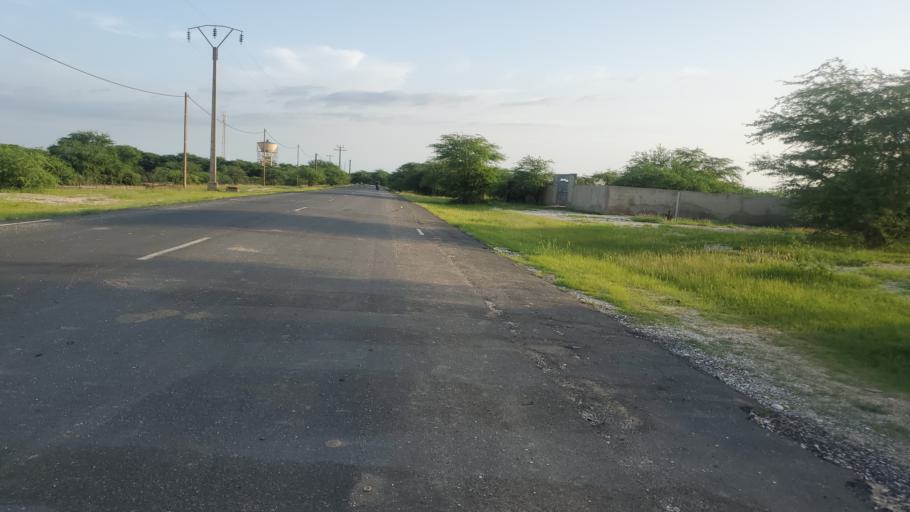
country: SN
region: Saint-Louis
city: Saint-Louis
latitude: 16.2115
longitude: -16.4154
